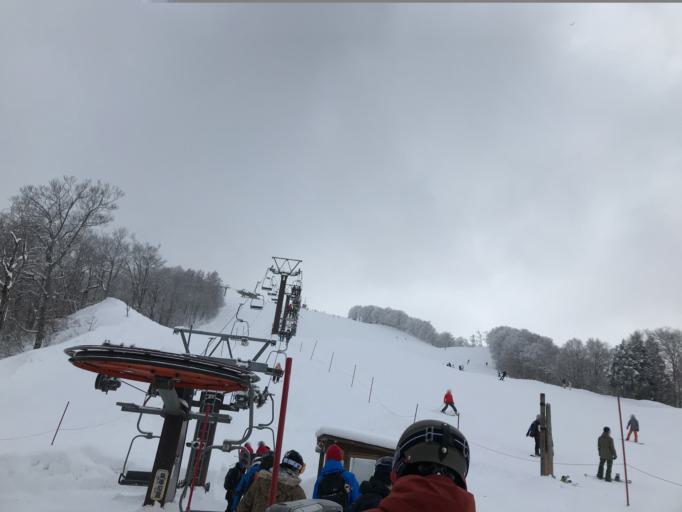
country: JP
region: Nagano
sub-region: Kitaazumi Gun
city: Hakuba
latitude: 36.7133
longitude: 137.8221
